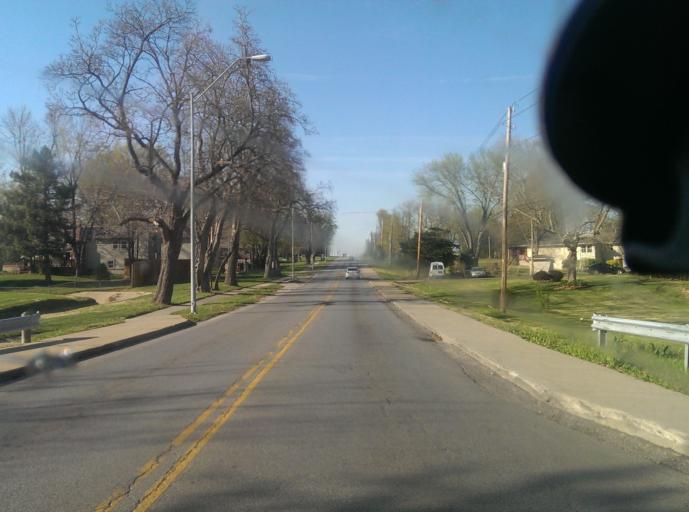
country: US
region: Missouri
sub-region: Jackson County
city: Grandview
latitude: 38.9129
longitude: -94.5844
